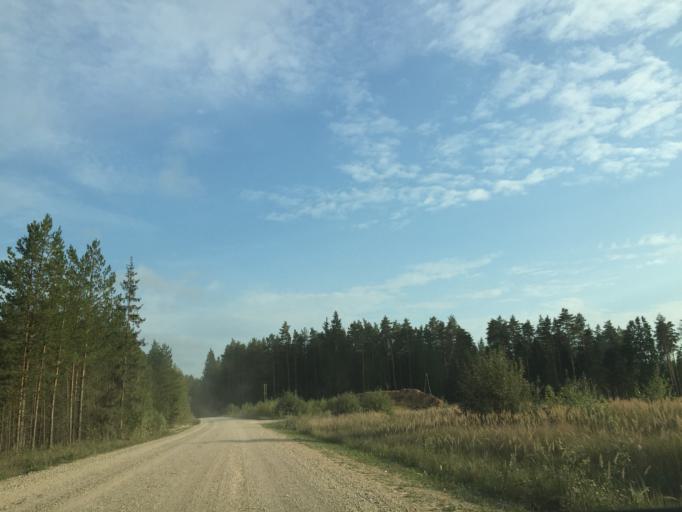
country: LV
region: Baldone
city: Baldone
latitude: 56.7913
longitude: 24.4404
